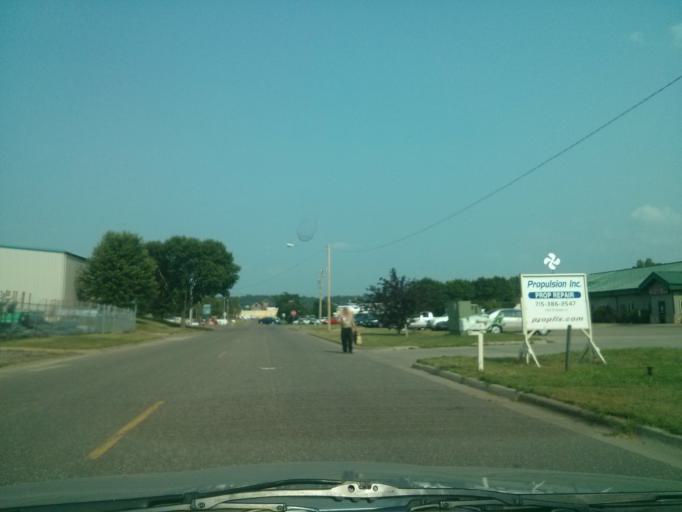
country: US
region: Wisconsin
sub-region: Saint Croix County
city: Hudson
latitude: 44.9603
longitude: -92.7328
